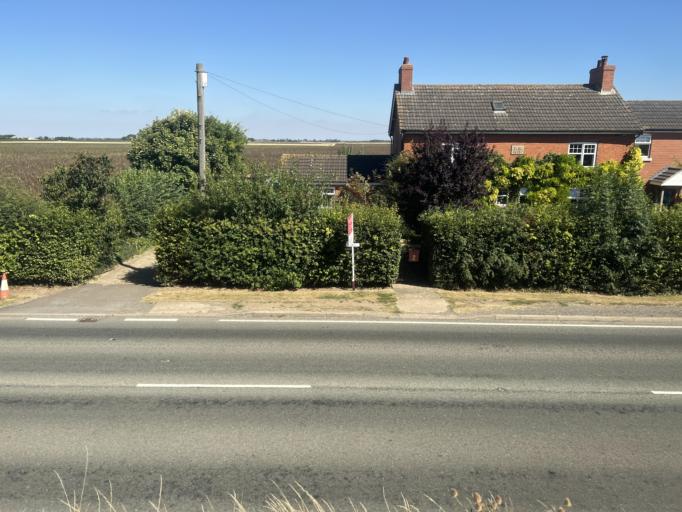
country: GB
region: England
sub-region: Lincolnshire
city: Kirton
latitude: 52.9750
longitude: -0.1028
